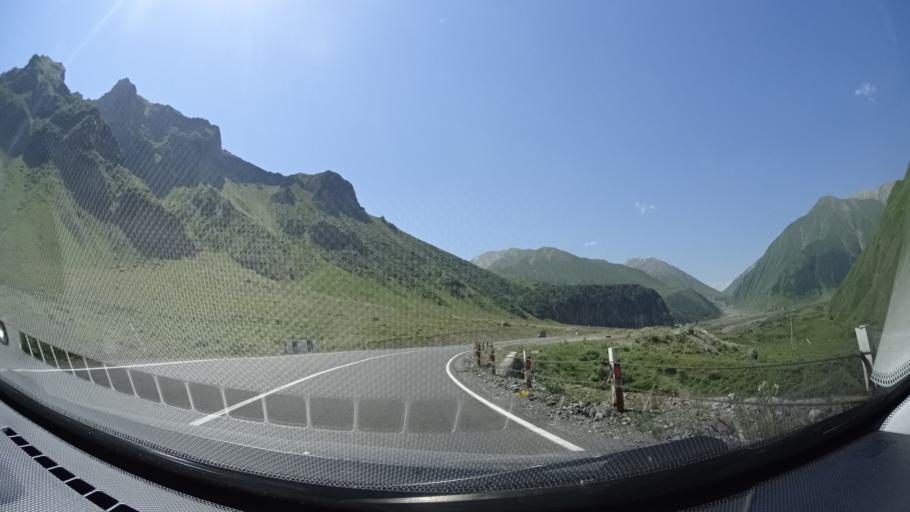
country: GE
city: Gudauri
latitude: 42.5751
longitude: 44.5249
